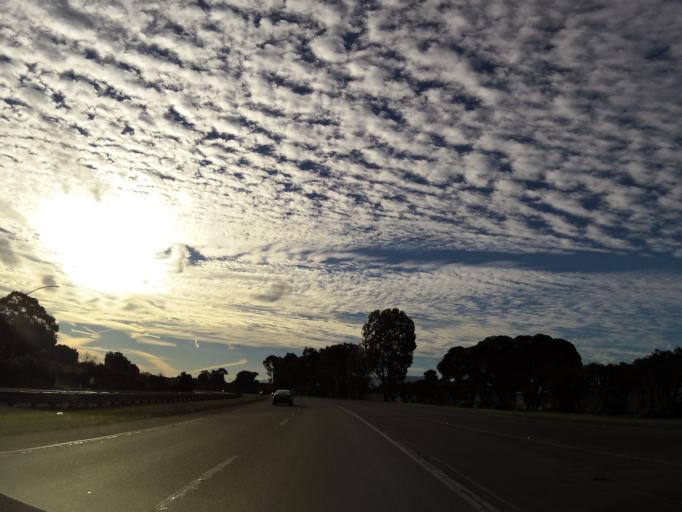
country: US
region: California
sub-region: Monterey County
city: Boronda
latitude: 36.6956
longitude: -121.6636
